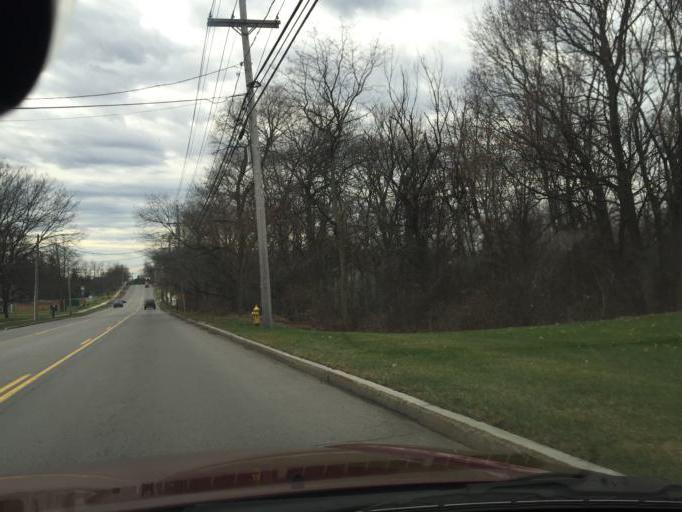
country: US
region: New York
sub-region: Monroe County
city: Rochester
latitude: 43.1200
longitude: -77.5954
